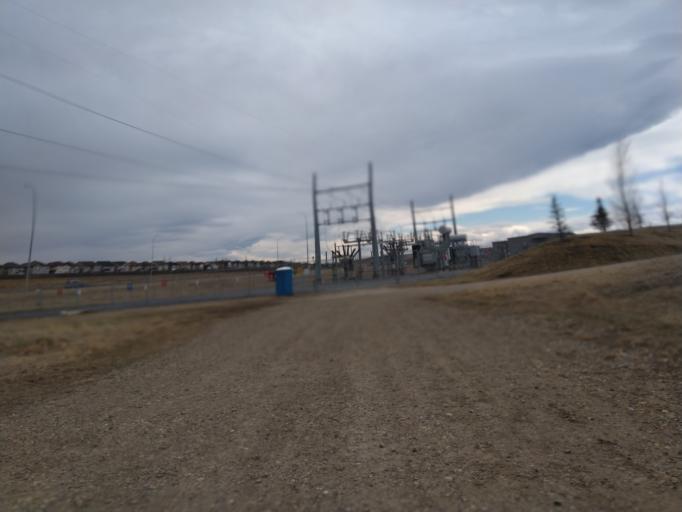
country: CA
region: Alberta
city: Calgary
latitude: 51.1688
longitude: -114.1059
